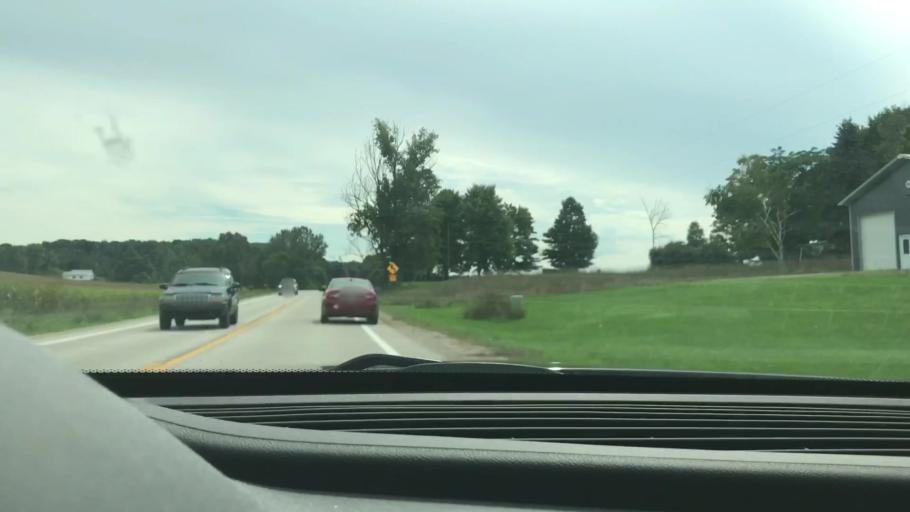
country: US
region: Michigan
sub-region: Antrim County
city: Bellaire
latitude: 45.0885
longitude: -85.2899
